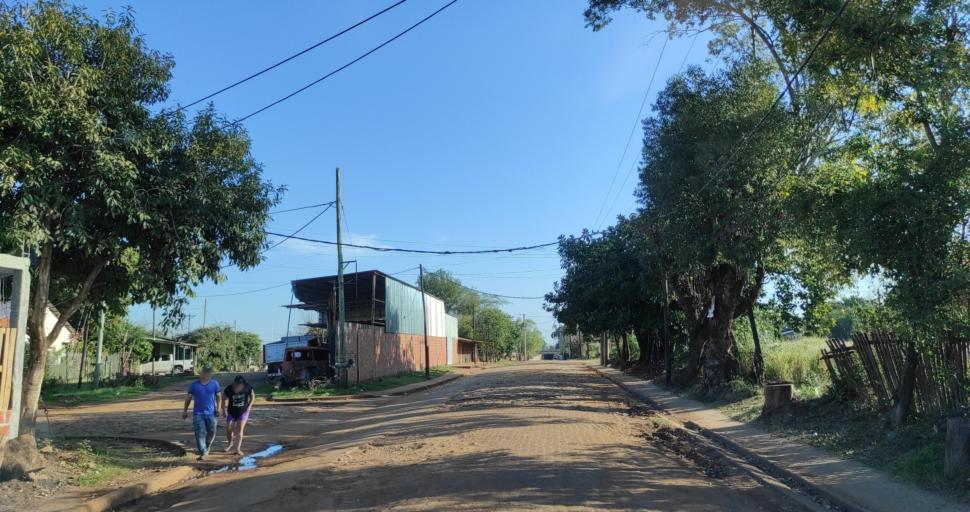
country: AR
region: Misiones
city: Garupa
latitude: -27.4503
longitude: -55.8632
